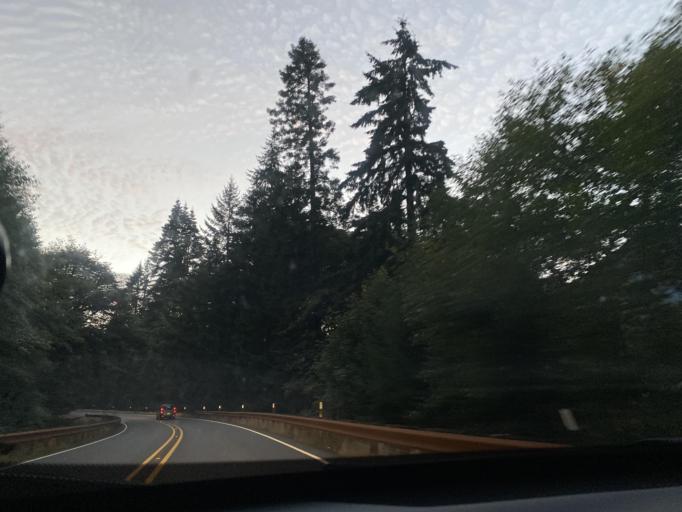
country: CA
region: British Columbia
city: Sooke
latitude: 48.0579
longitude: -123.7856
